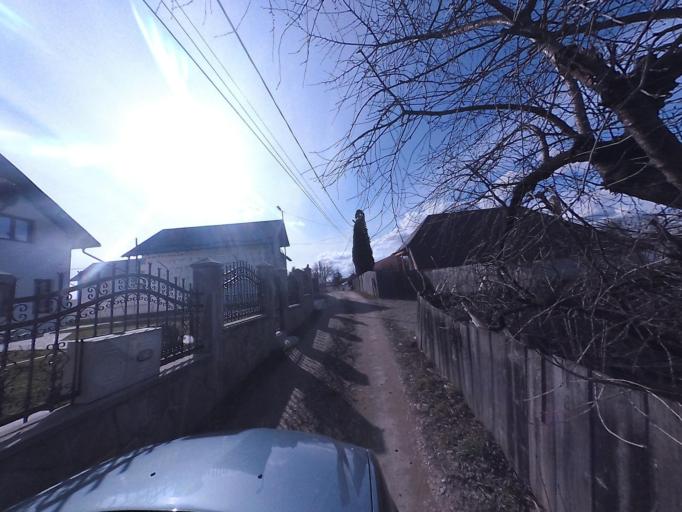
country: RO
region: Neamt
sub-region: Oras Targu Neamt
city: Humulesti
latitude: 47.2010
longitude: 26.3527
